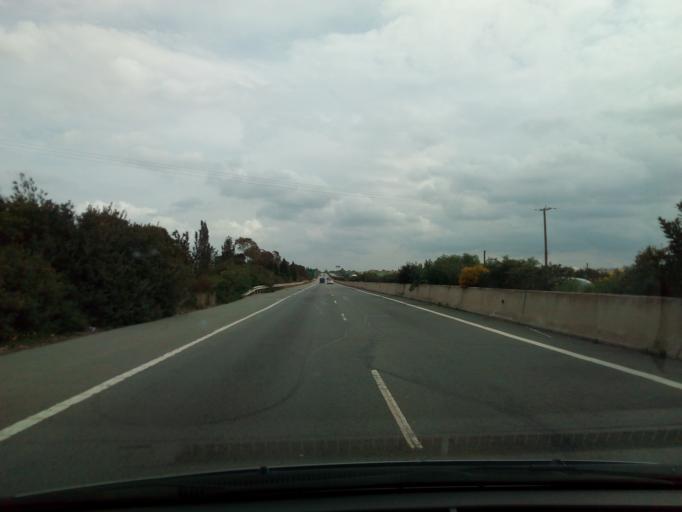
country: CY
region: Lefkosia
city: Kato Deftera
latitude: 35.1351
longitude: 33.2825
